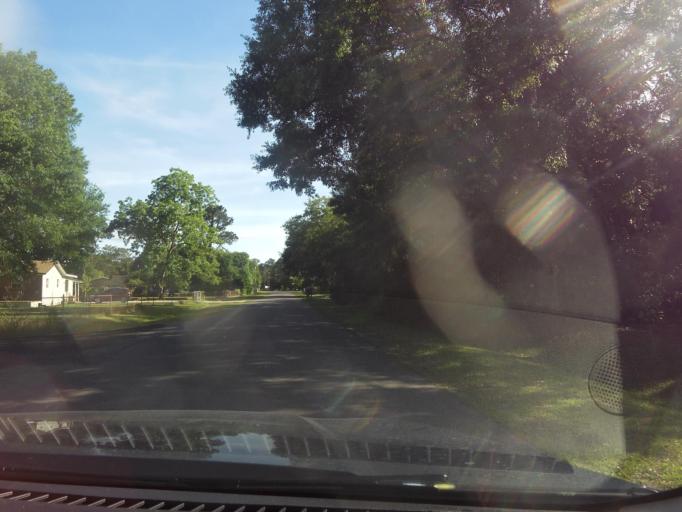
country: US
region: Florida
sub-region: Nassau County
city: Nassau Village-Ratliff
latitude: 30.5209
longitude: -81.7721
